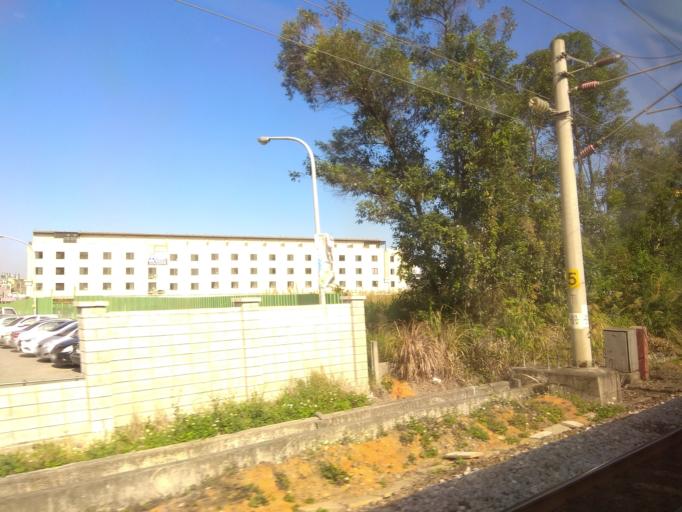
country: TW
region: Taiwan
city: Taoyuan City
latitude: 24.9670
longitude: 121.2489
